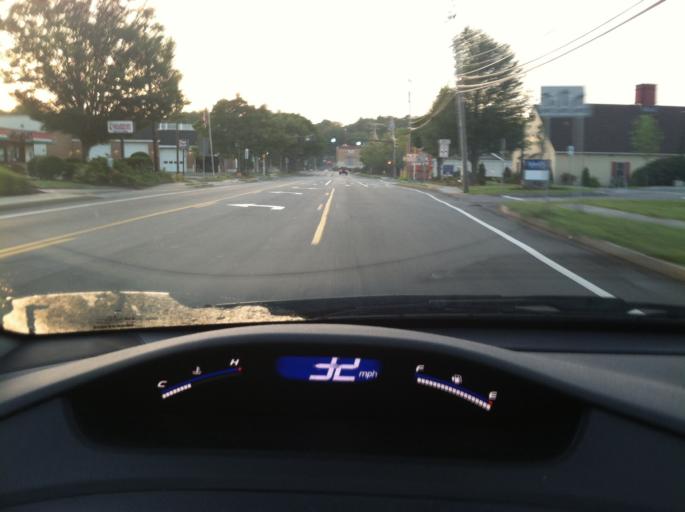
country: US
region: Massachusetts
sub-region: Middlesex County
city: Bedford
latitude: 42.4870
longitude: -71.2640
